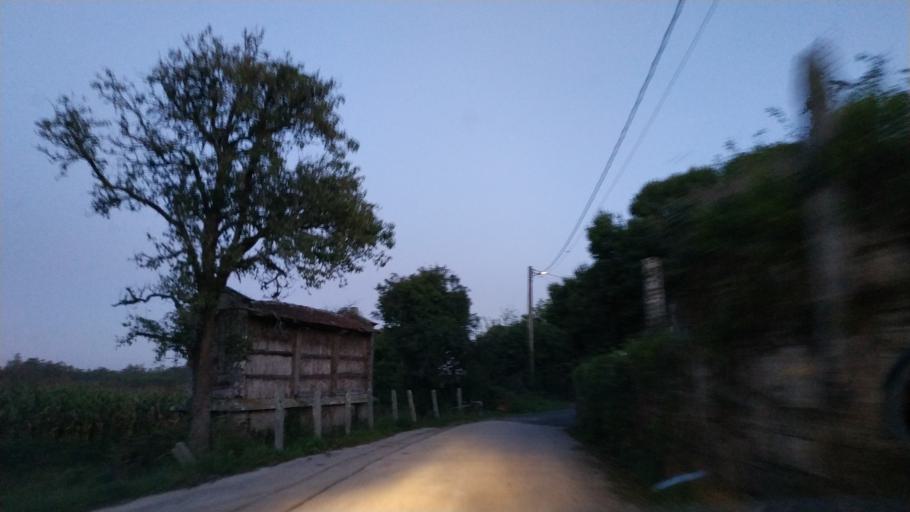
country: ES
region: Galicia
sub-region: Provincia da Coruna
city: Negreira
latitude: 42.9112
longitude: -8.7639
